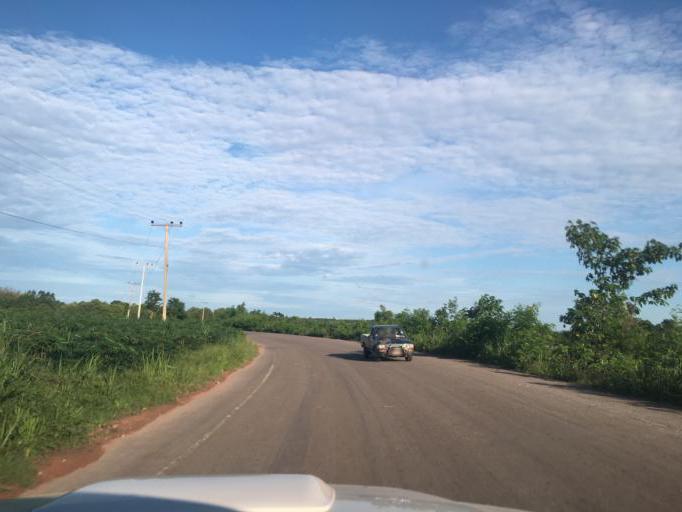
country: TH
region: Changwat Udon Thani
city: Udon Thani
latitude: 17.3022
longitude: 102.6749
